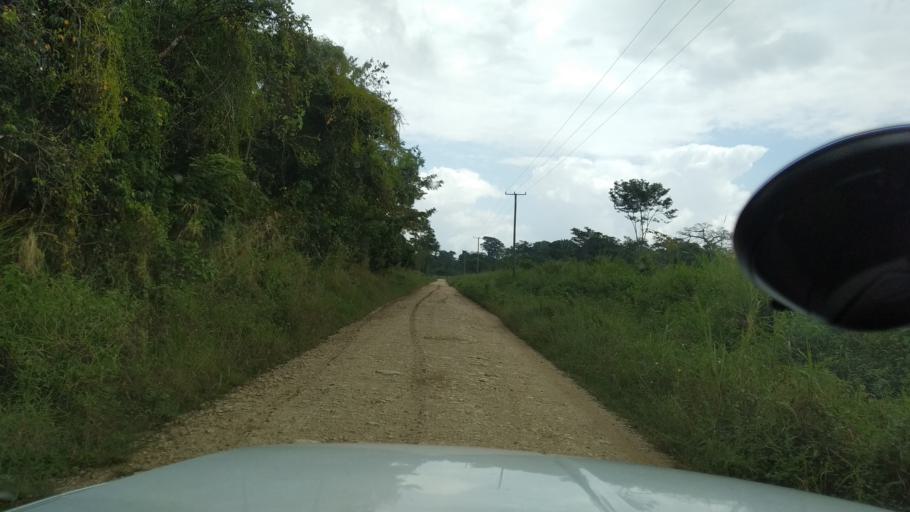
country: BZ
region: Toledo
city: Punta Gorda
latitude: 16.2199
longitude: -88.9965
